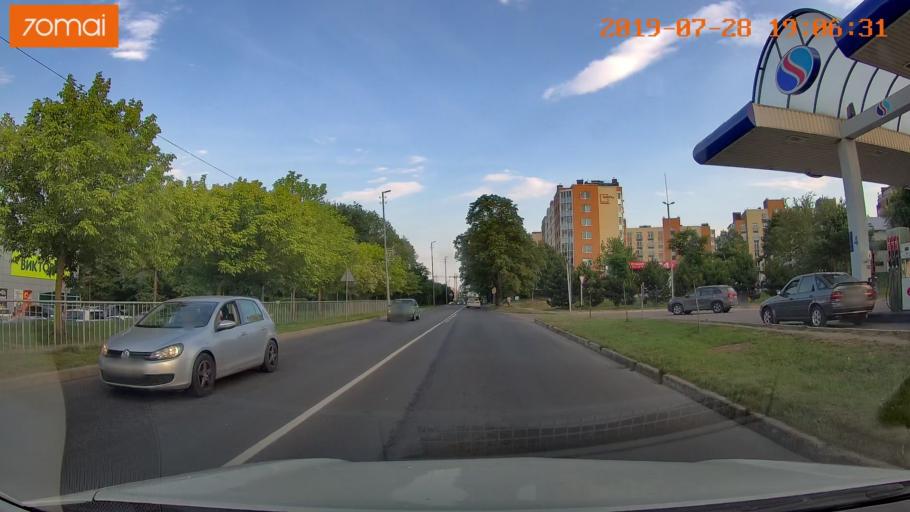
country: RU
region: Kaliningrad
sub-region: Gorod Svetlogorsk
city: Svetlogorsk
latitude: 54.9309
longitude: 20.1656
